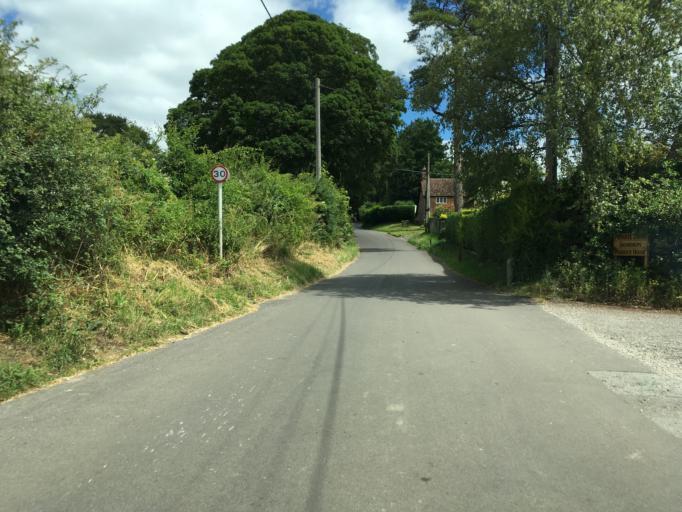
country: GB
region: England
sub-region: Hampshire
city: Highclere
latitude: 51.2658
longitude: -1.4214
